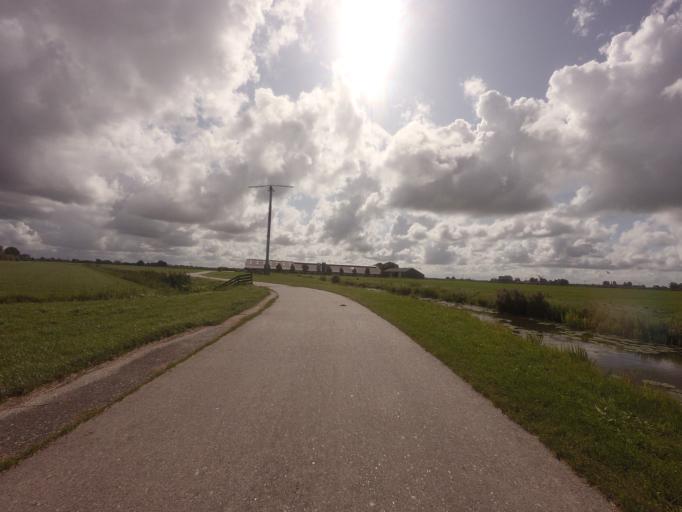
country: NL
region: Friesland
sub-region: Sudwest Fryslan
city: Scharnegoutum
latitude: 53.0735
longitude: 5.6370
